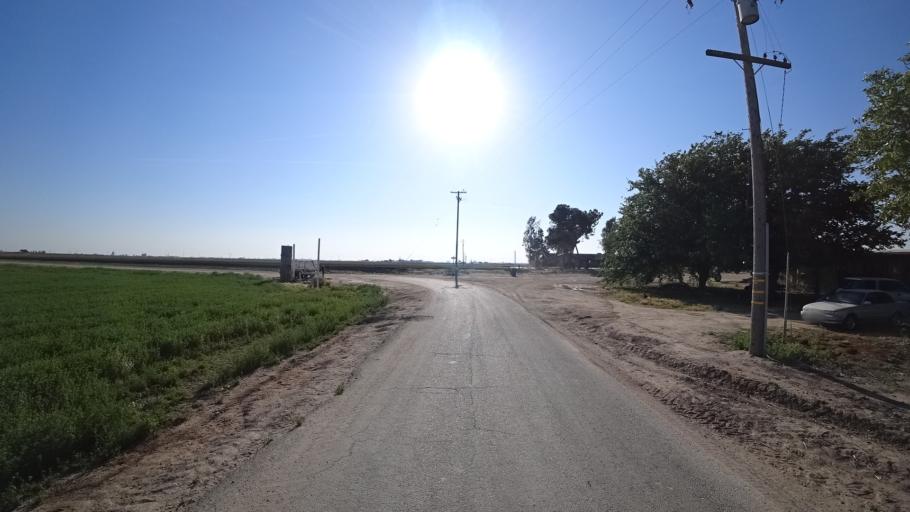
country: US
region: California
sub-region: Fresno County
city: Riverdale
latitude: 36.4016
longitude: -119.9145
